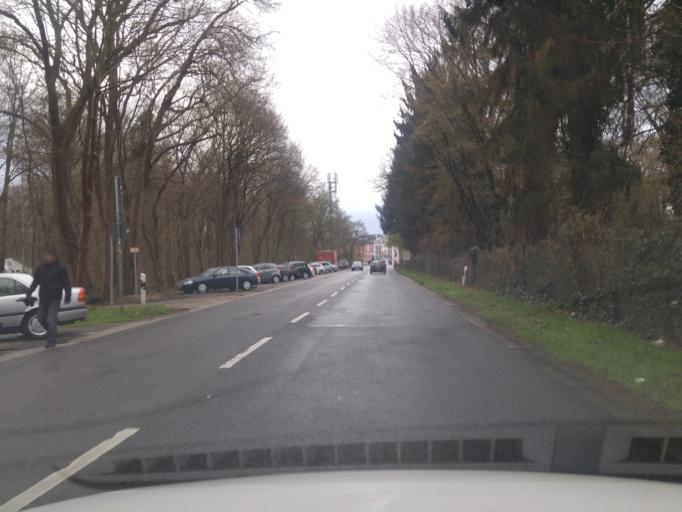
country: DE
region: North Rhine-Westphalia
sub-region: Regierungsbezirk Koln
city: Buchheim
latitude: 50.9457
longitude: 7.0279
